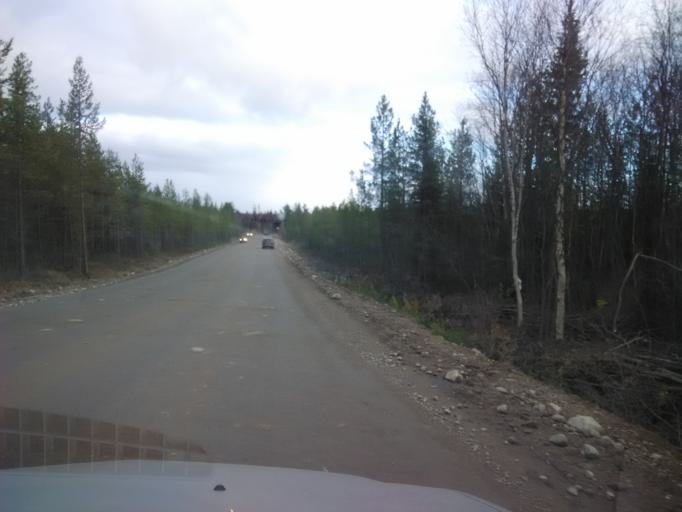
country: RU
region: Murmansk
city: Polyarnyye Zori
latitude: 67.3751
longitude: 32.5101
